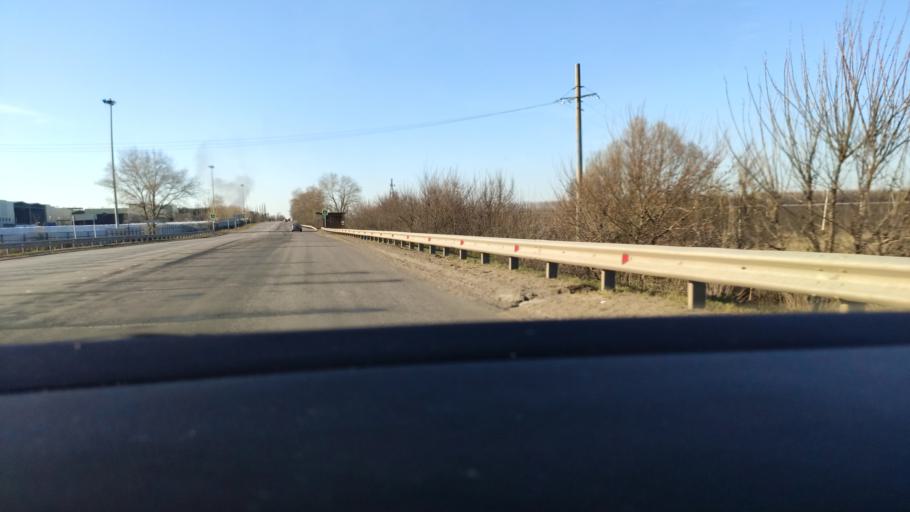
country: RU
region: Voronezj
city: Maslovka
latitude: 51.5511
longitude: 39.2814
